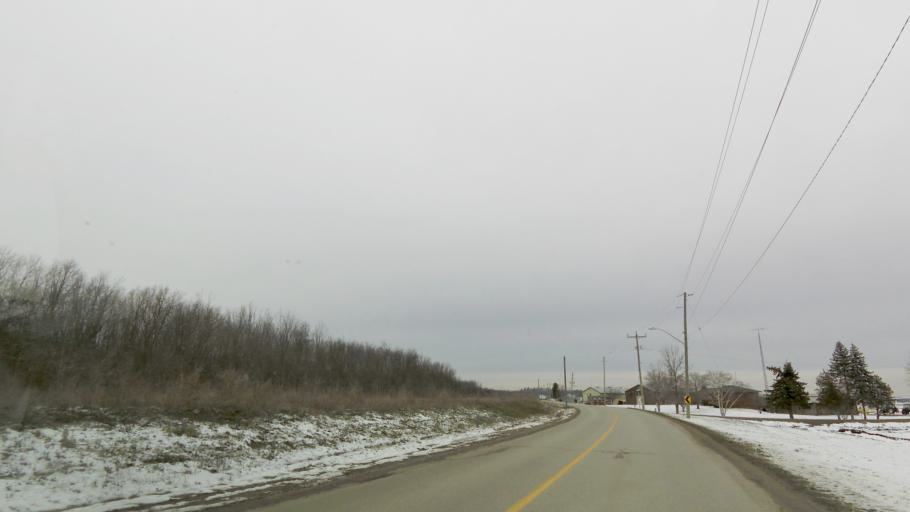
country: CA
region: Ontario
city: Bradford West Gwillimbury
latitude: 44.0661
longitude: -79.5895
